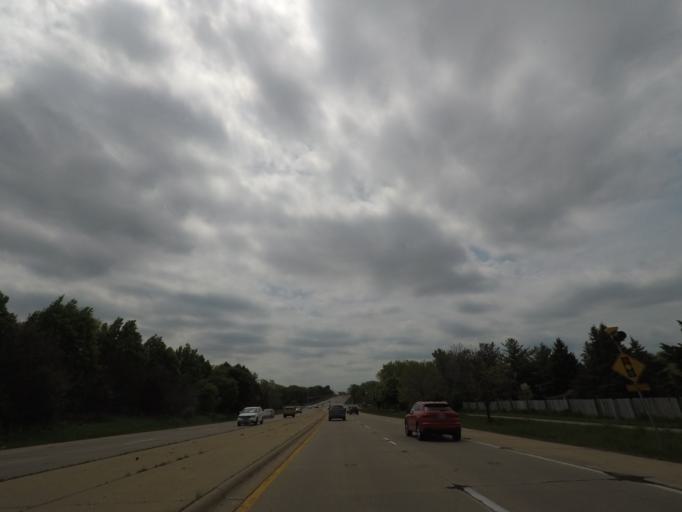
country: US
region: Illinois
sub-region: Winnebago County
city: Cherry Valley
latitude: 42.2852
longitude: -88.9803
